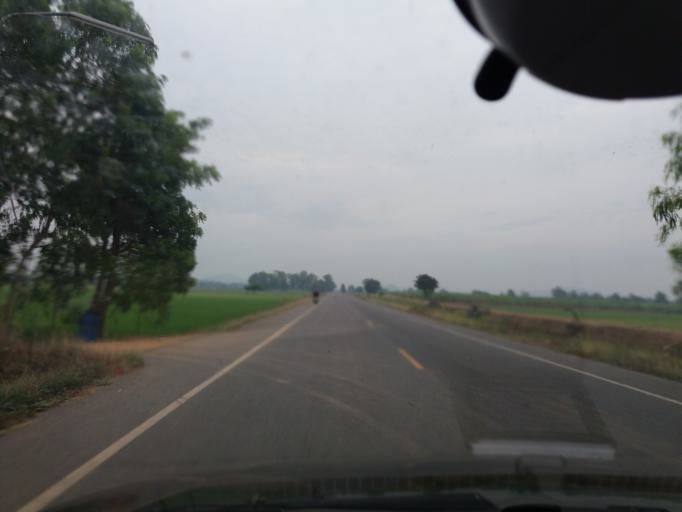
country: TH
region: Suphan Buri
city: Doem Bang Nang Buat
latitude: 14.8695
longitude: 100.1322
